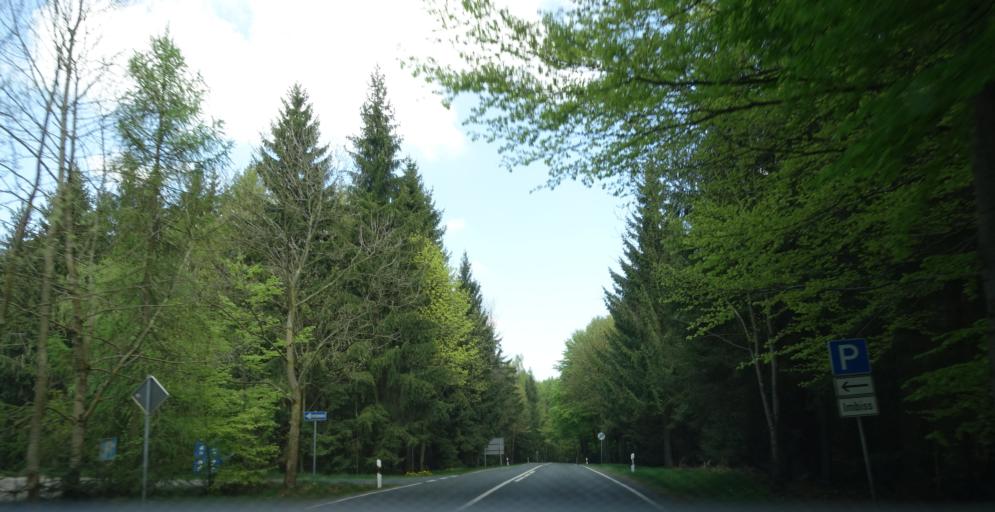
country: DE
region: Saxony
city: Grosshartmannsdorf
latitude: 50.8246
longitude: 13.3266
